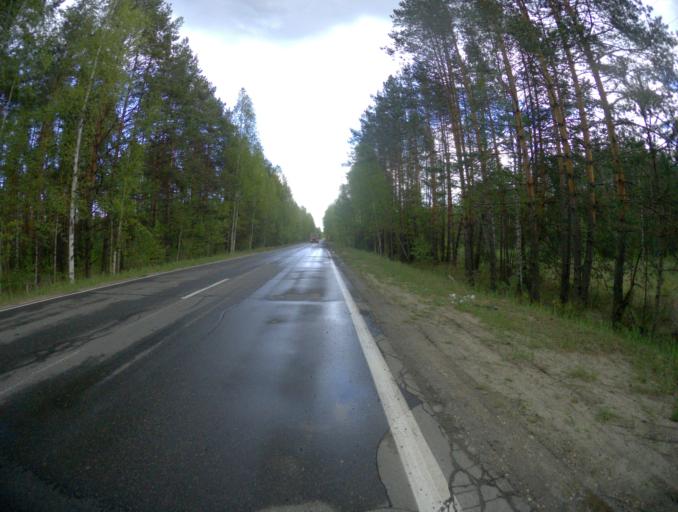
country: RU
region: Vladimir
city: Mezinovskiy
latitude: 55.5951
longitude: 40.3857
